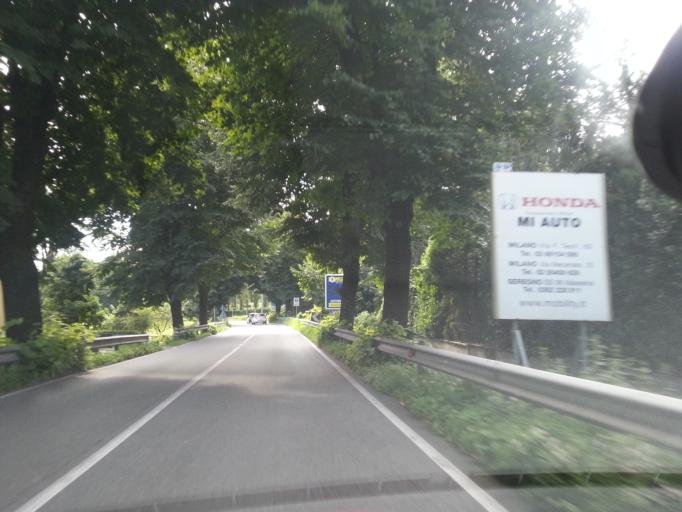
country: IT
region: Lombardy
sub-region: Provincia di Monza e Brianza
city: Villa Raverio
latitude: 45.6963
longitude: 9.2753
